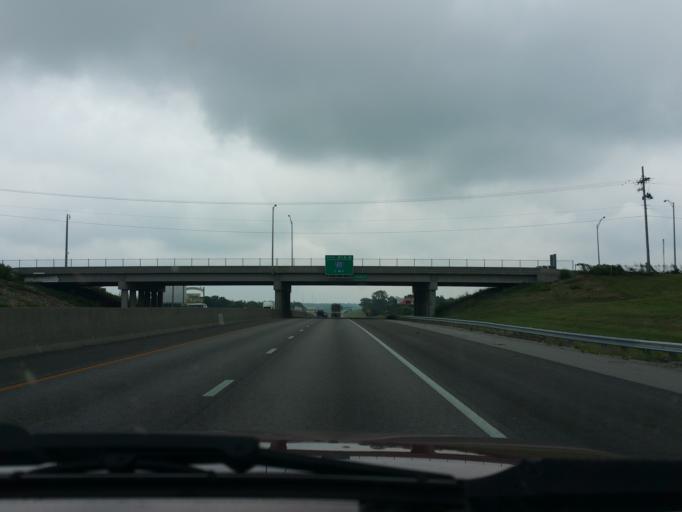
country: US
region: Kansas
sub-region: Wyandotte County
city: Edwardsville
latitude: 39.1058
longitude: -94.8365
